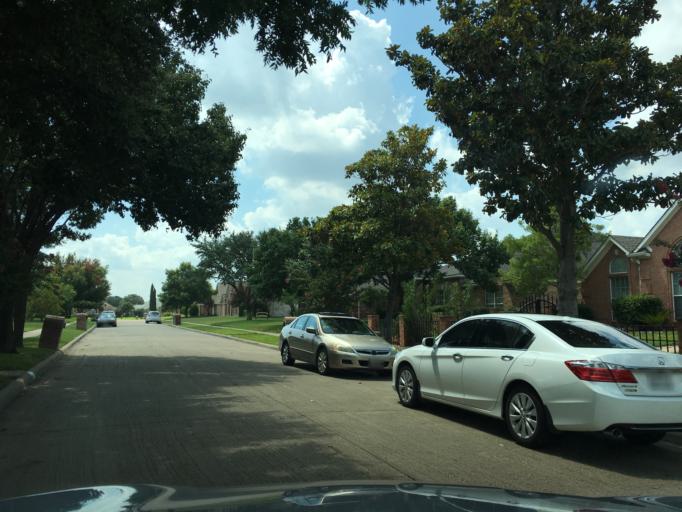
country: US
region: Texas
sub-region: Dallas County
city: Garland
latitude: 32.9429
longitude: -96.6463
